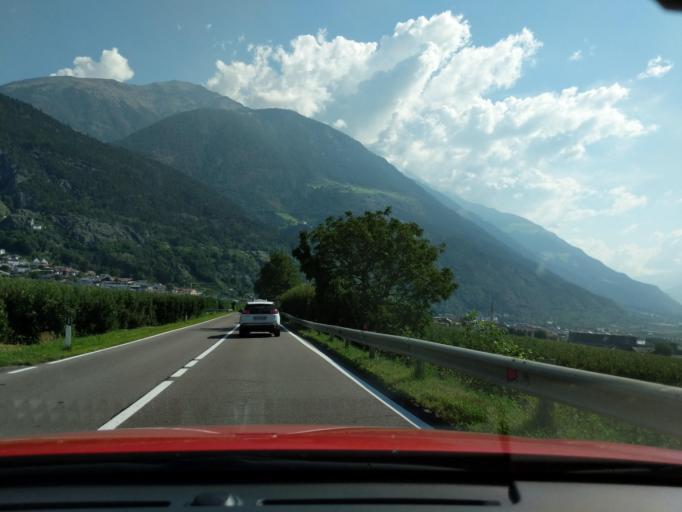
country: IT
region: Trentino-Alto Adige
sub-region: Bolzano
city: Silandro
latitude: 46.6245
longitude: 10.7558
